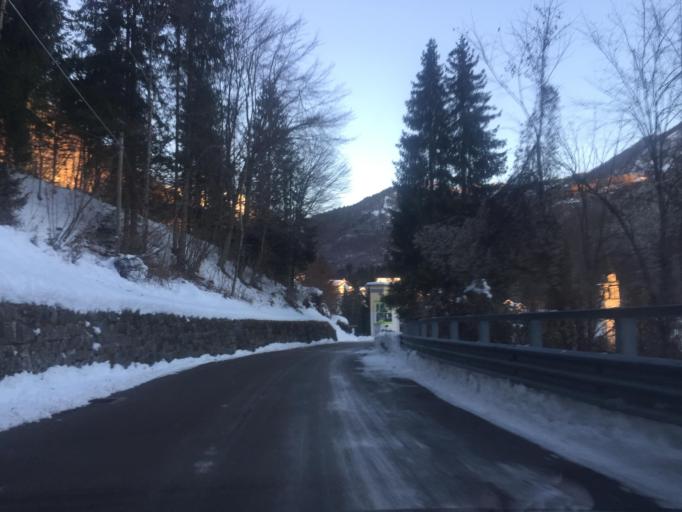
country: IT
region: Friuli Venezia Giulia
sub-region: Provincia di Udine
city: Lauco
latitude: 46.4385
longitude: 12.9471
